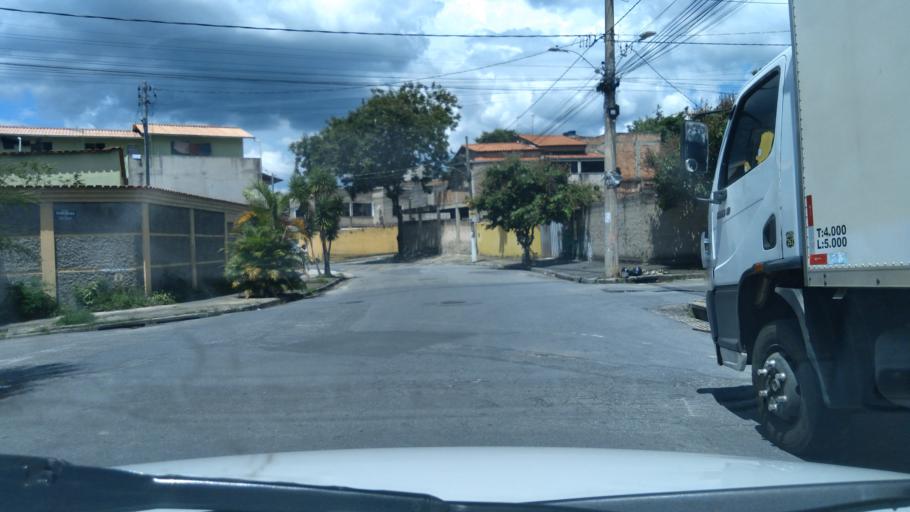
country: BR
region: Minas Gerais
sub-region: Belo Horizonte
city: Belo Horizonte
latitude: -19.8587
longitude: -43.8725
